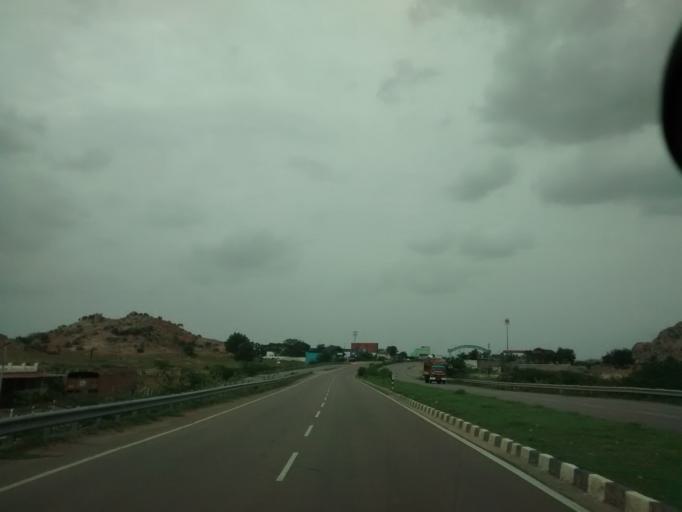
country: IN
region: Andhra Pradesh
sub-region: Kurnool
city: Ramapuram
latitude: 15.1620
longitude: 77.6741
